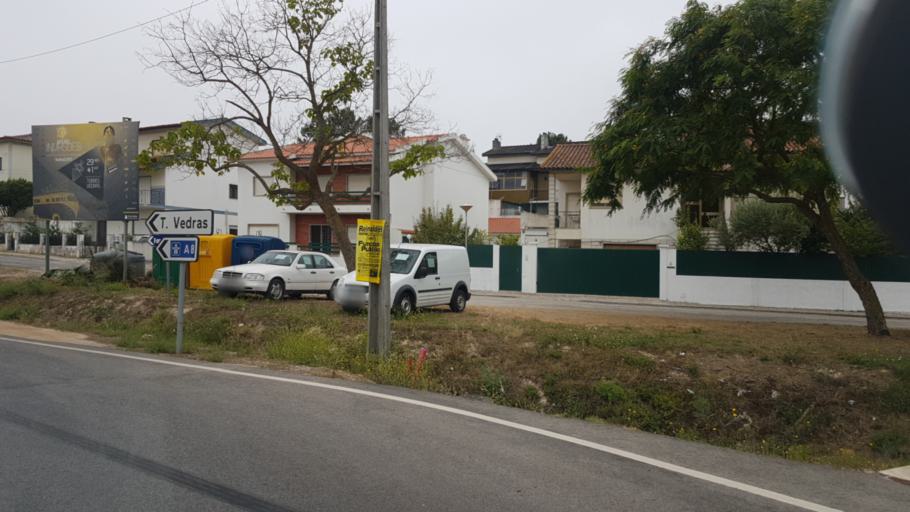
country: PT
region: Lisbon
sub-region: Torres Vedras
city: Torres Vedras
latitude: 39.1062
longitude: -9.2592
